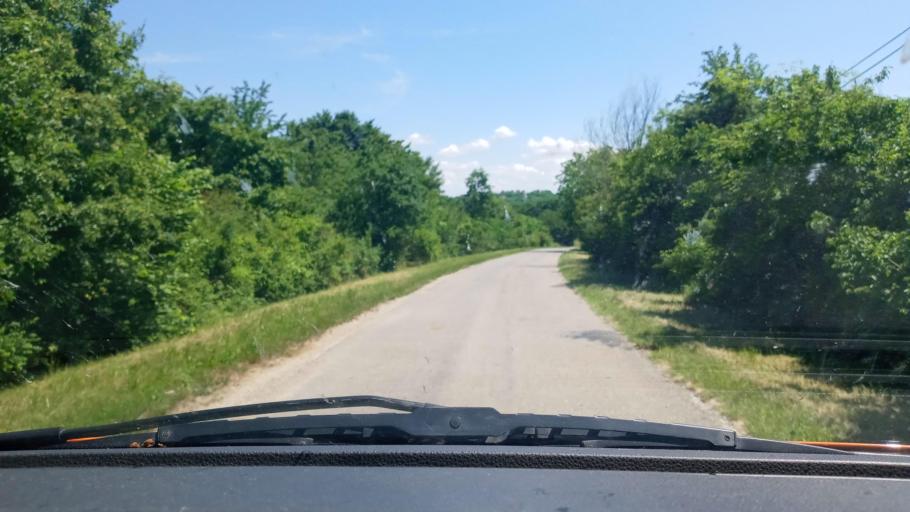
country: HU
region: Baranya
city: Szigetvar
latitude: 46.1726
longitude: 17.7503
